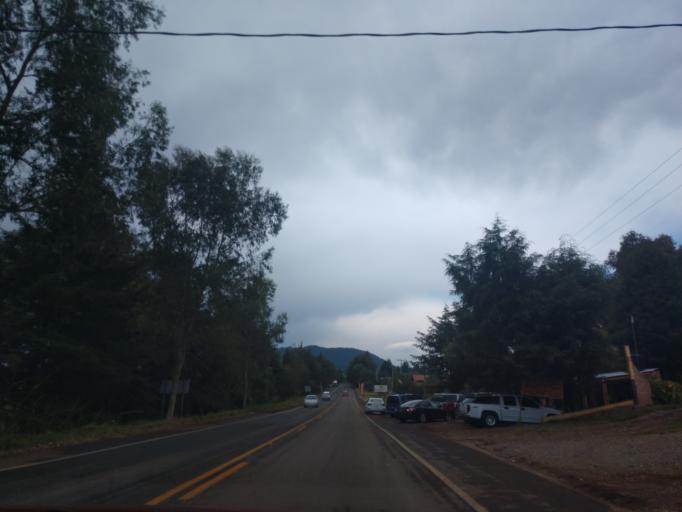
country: MX
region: Jalisco
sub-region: Mazamitla
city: Mazamitla
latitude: 19.9333
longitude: -103.0420
